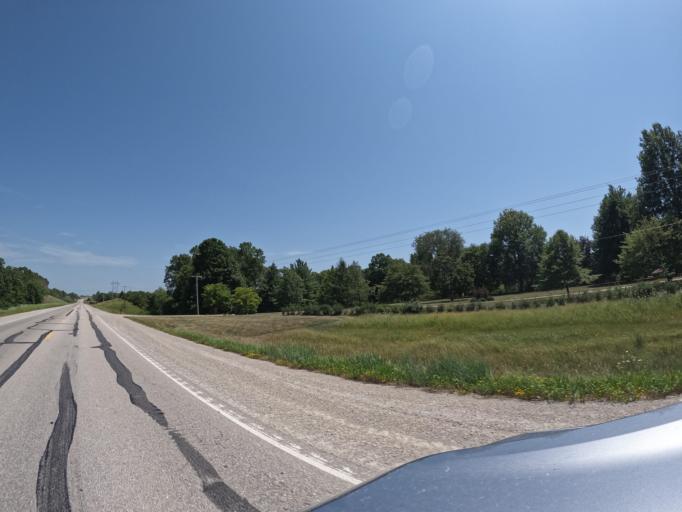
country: US
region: Iowa
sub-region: Henry County
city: Mount Pleasant
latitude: 40.9672
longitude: -91.6089
